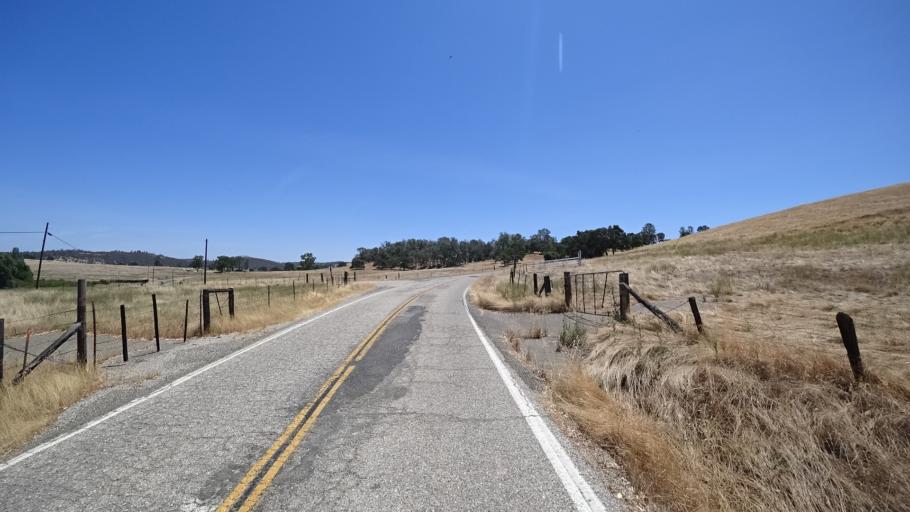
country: US
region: California
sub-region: Calaveras County
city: Valley Springs
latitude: 38.2283
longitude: -120.8377
